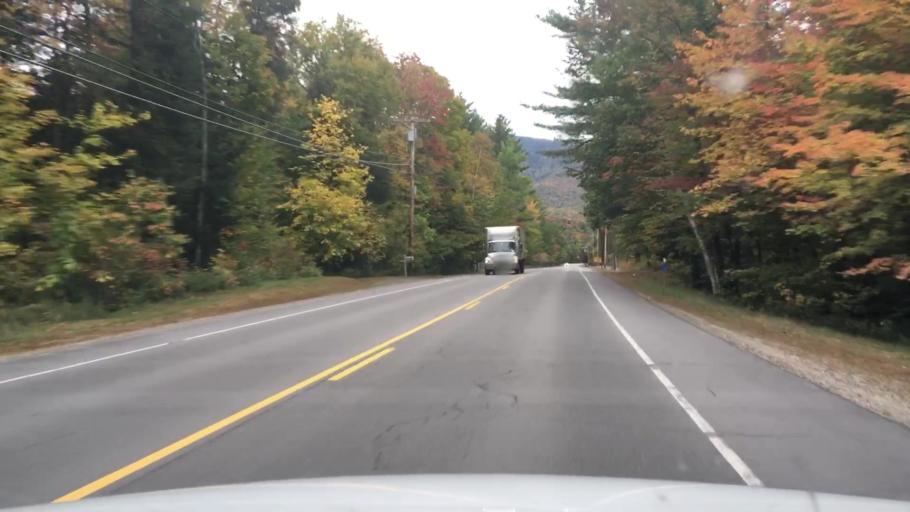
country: US
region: New Hampshire
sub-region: Coos County
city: Gorham
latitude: 44.3717
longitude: -71.1747
